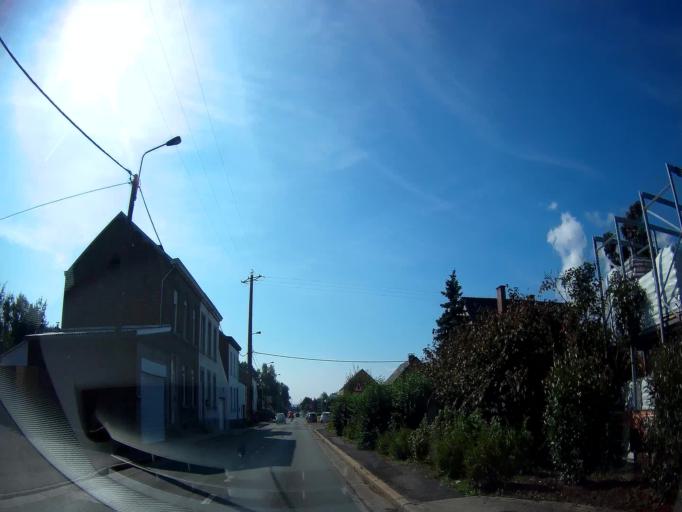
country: BE
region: Wallonia
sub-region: Province de Liege
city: Amay
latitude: 50.5588
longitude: 5.3056
